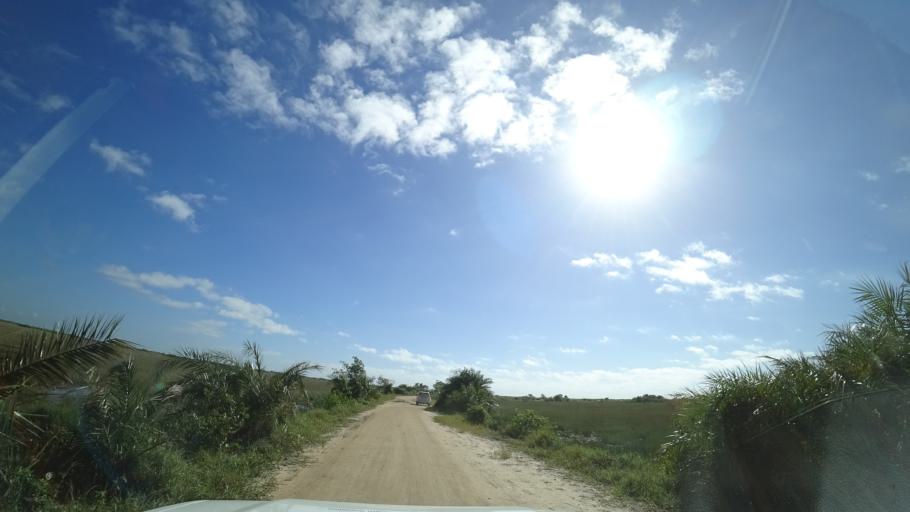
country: MZ
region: Sofala
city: Beira
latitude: -19.7076
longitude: 35.0176
